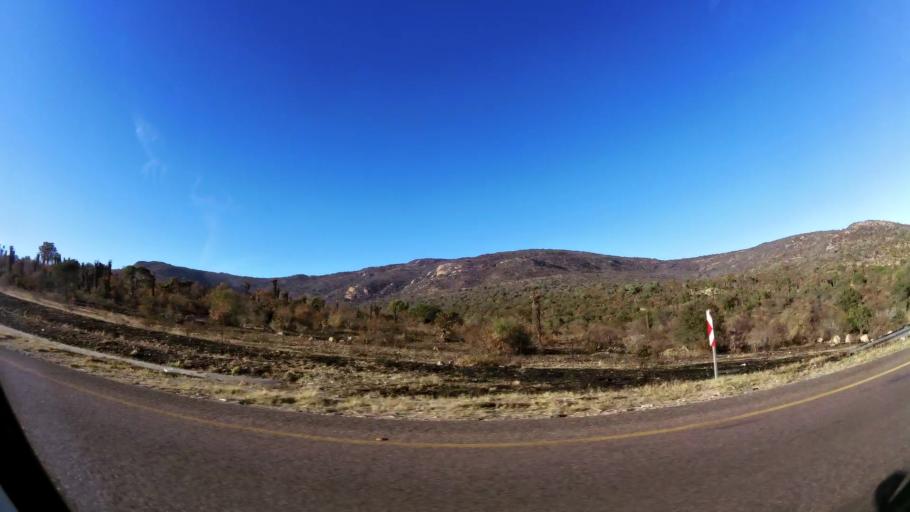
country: ZA
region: Limpopo
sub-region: Capricorn District Municipality
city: Mankoeng
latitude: -23.9315
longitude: 29.8489
